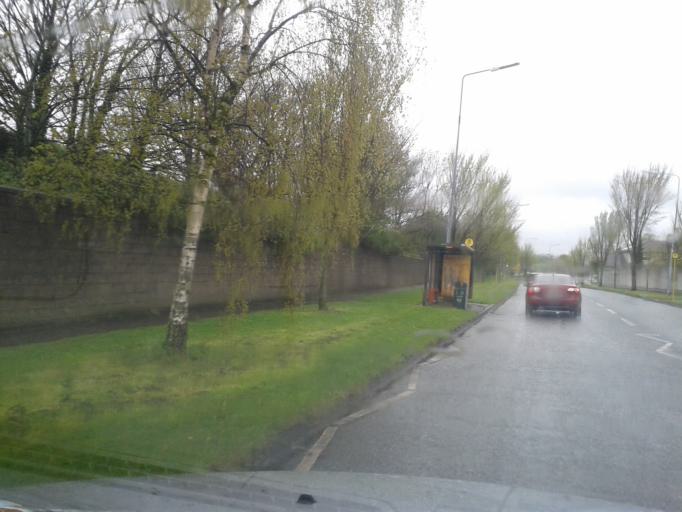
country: IE
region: Leinster
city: Templeogue
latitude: 53.2954
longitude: -6.3225
